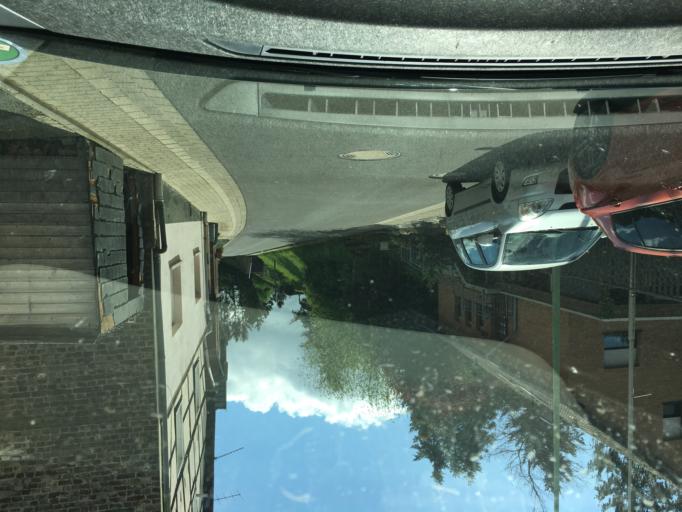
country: DE
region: North Rhine-Westphalia
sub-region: Regierungsbezirk Koln
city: Vettweiss
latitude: 50.6889
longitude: 6.6065
